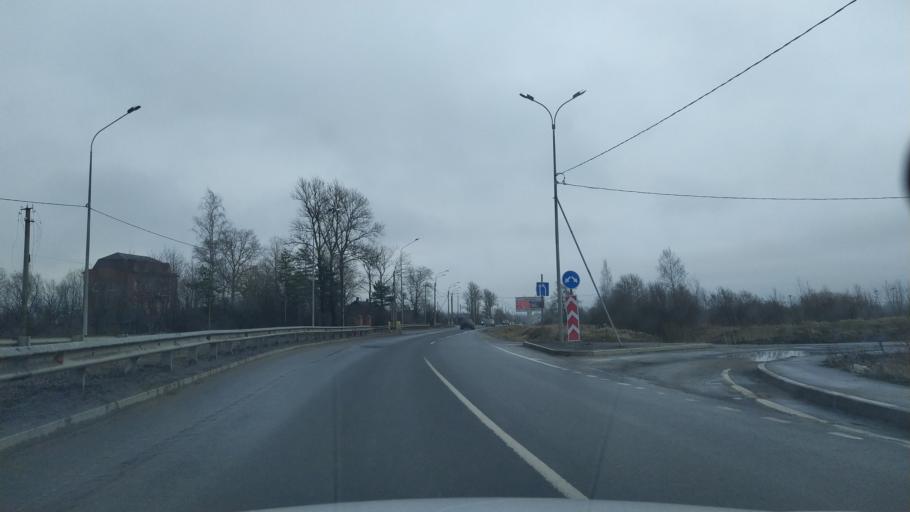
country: RU
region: St.-Petersburg
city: Aleksandrovskaya
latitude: 59.7155
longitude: 30.2945
